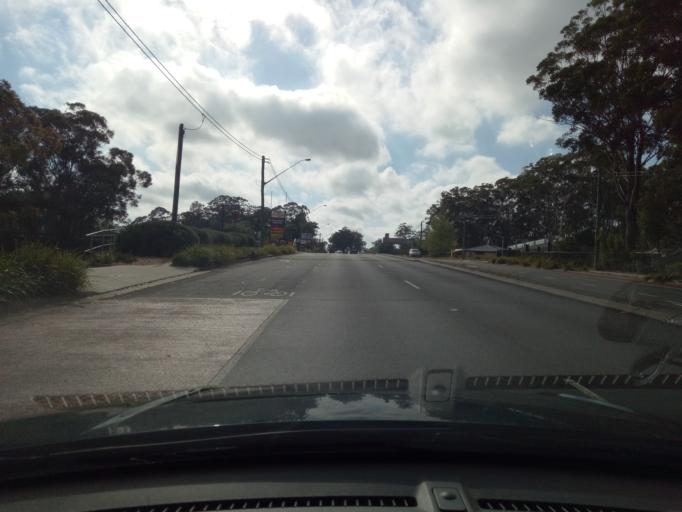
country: AU
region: New South Wales
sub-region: Gosford Shire
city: Erina
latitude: -33.4258
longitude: 151.3996
